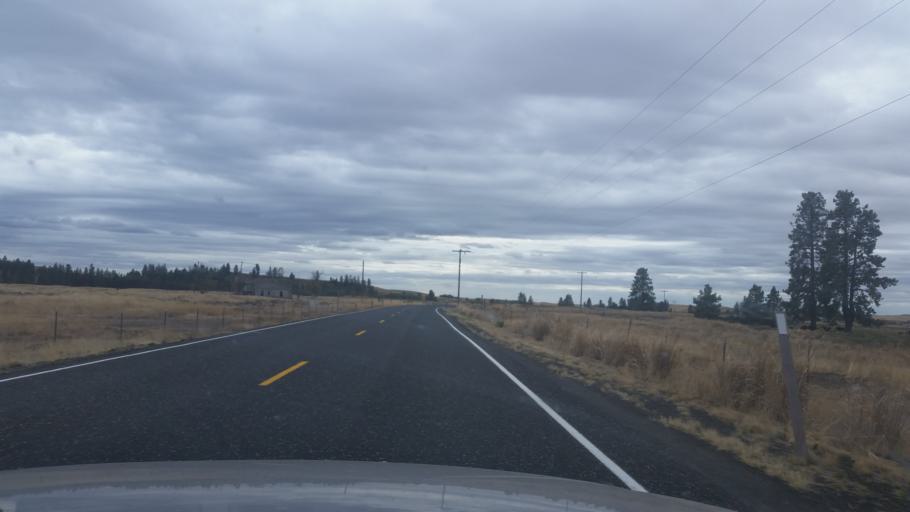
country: US
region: Washington
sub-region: Spokane County
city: Medical Lake
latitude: 47.5307
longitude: -117.8436
